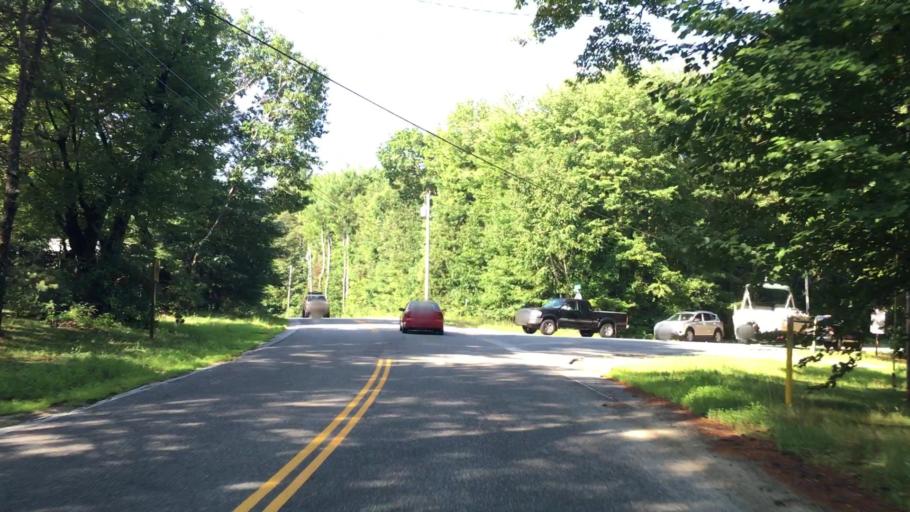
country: US
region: Maine
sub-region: Androscoggin County
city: Minot
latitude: 44.0431
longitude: -70.3355
